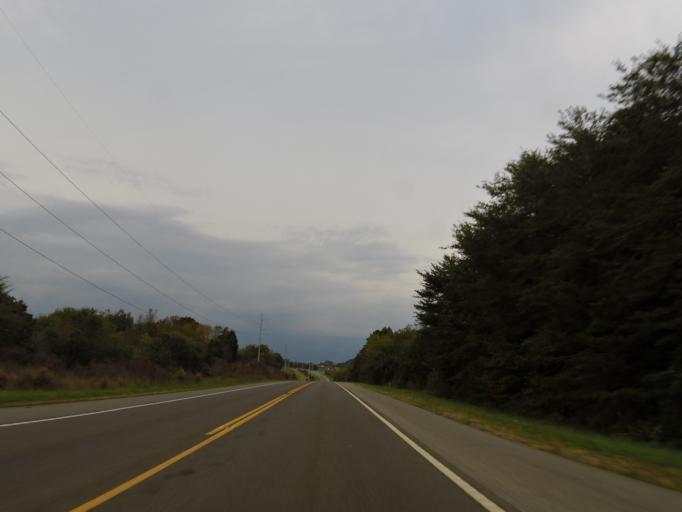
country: US
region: Tennessee
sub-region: Monroe County
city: Vonore
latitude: 35.6520
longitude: -84.2865
